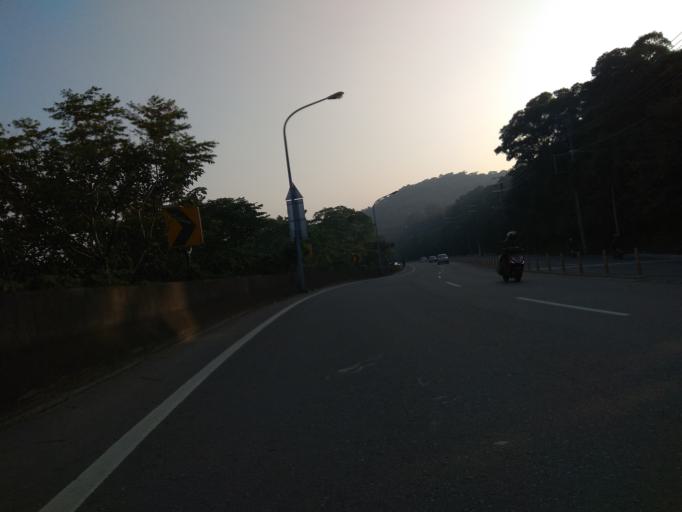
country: TW
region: Taiwan
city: Daxi
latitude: 24.9100
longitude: 121.1887
